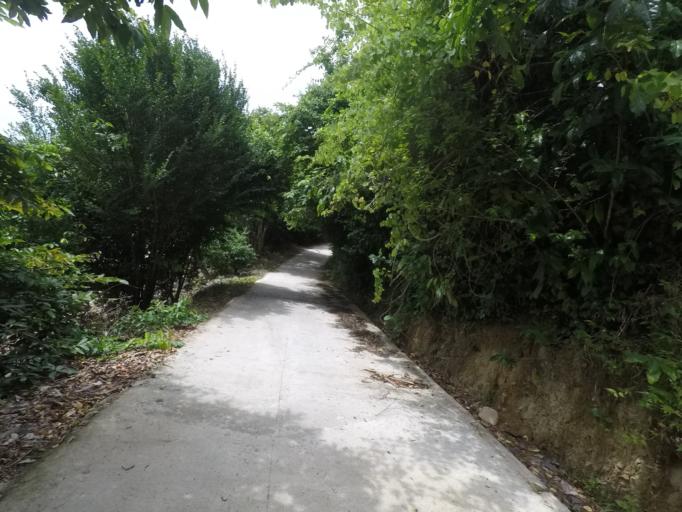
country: TH
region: Phangnga
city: Ban Phru Nai
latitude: 7.7666
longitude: 98.7711
